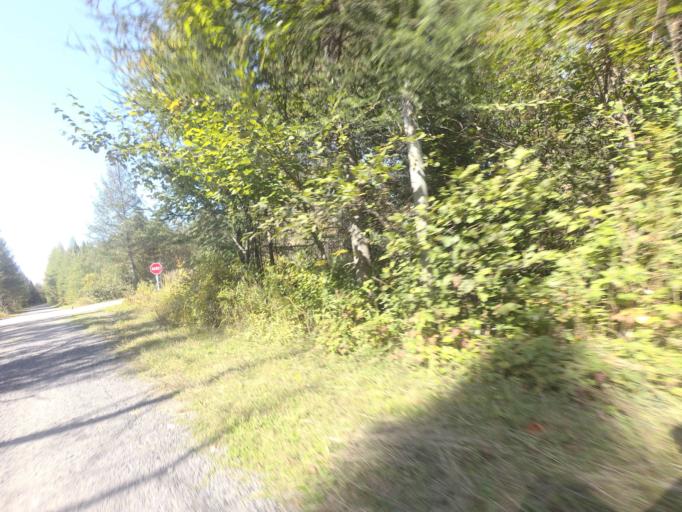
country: CA
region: Quebec
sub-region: Laurentides
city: Sainte-Agathe-des-Monts
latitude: 46.1040
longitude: -74.3807
